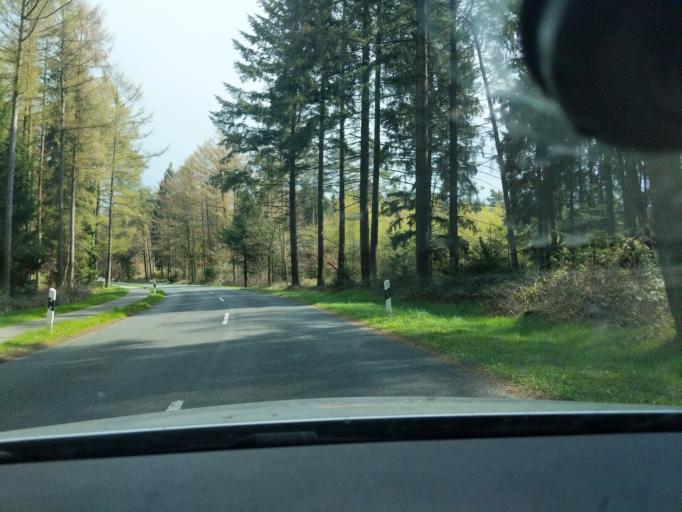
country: DE
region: Lower Saxony
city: Dollern
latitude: 53.5141
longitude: 9.5264
